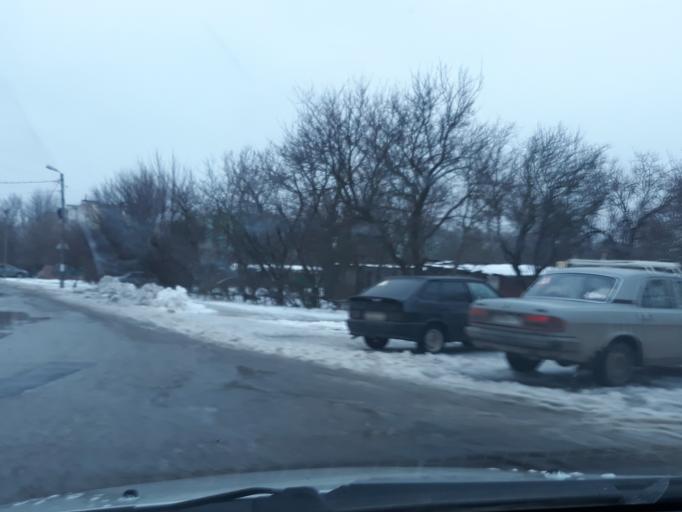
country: RU
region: Rostov
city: Taganrog
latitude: 47.2410
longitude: 38.8667
